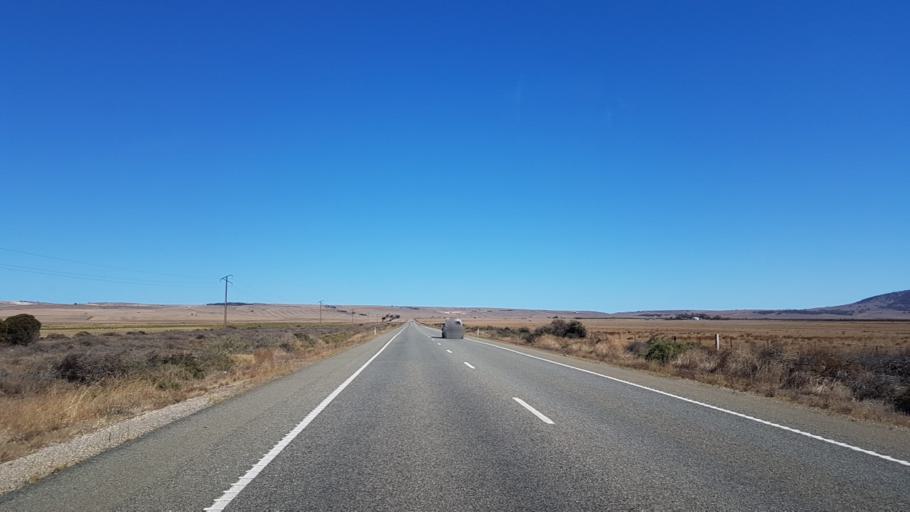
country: AU
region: South Australia
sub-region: Wakefield
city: Balaklava
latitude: -34.0855
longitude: 138.0876
